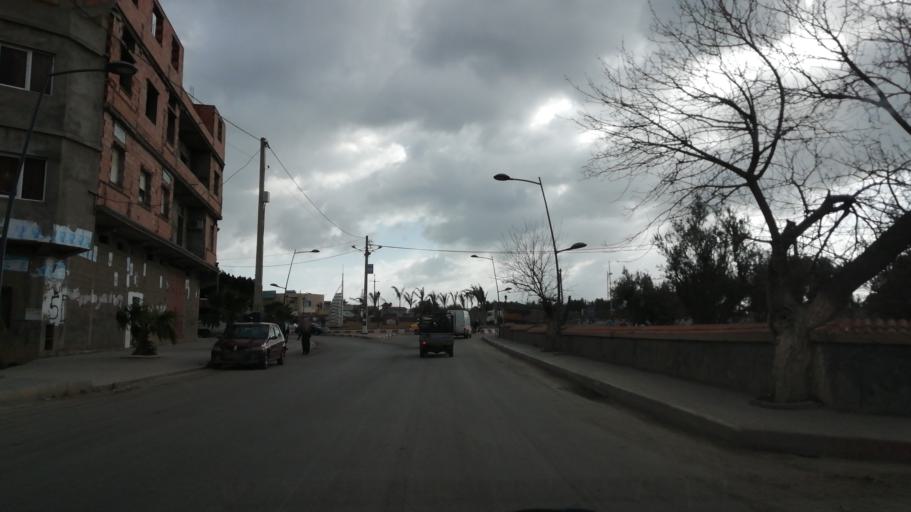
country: DZ
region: Oran
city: Sidi ech Chahmi
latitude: 35.6564
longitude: -0.5260
